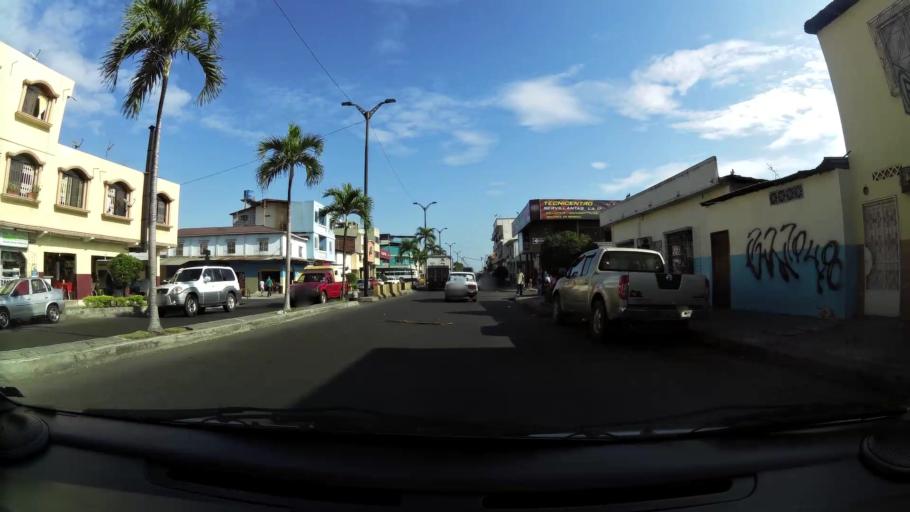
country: EC
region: Guayas
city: Guayaquil
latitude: -2.1959
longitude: -79.9142
